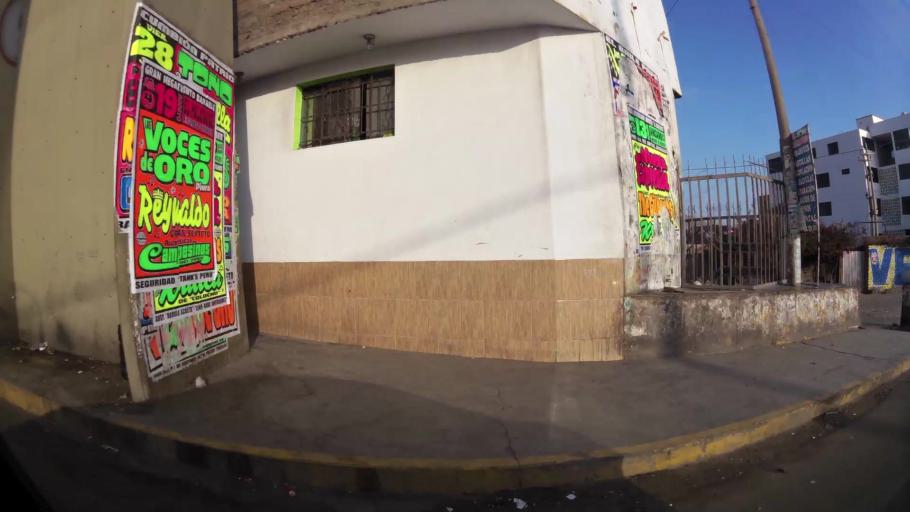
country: PE
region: La Libertad
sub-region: Provincia de Trujillo
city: El Porvenir
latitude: -8.0874
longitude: -79.0047
